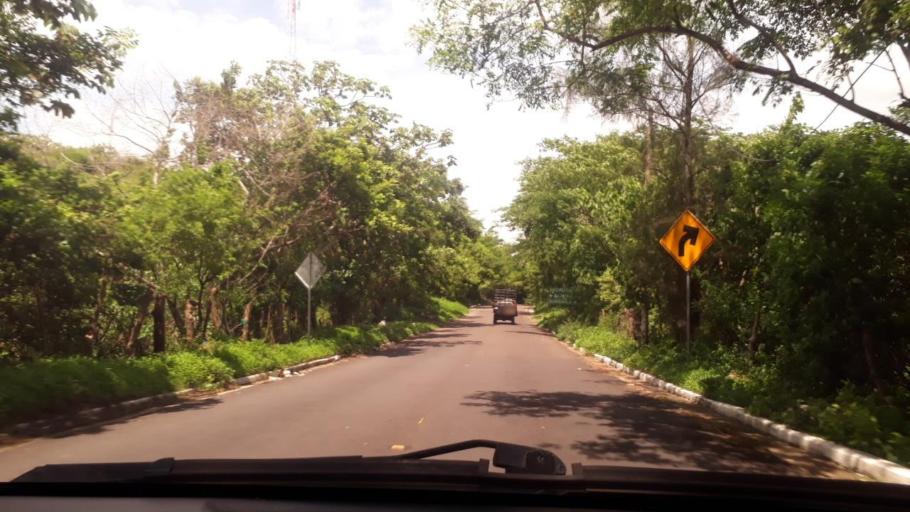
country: GT
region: Jutiapa
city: Jalpatagua
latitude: 14.1637
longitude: -90.0504
